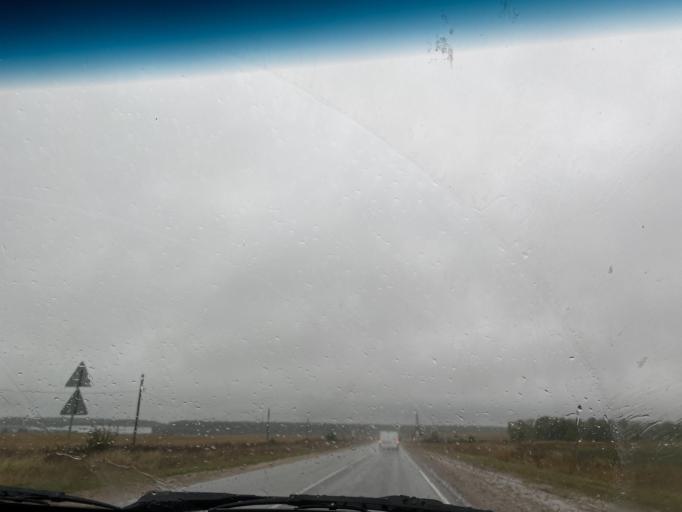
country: RU
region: Rjazan
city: Ryazan'
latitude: 54.4870
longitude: 39.8186
